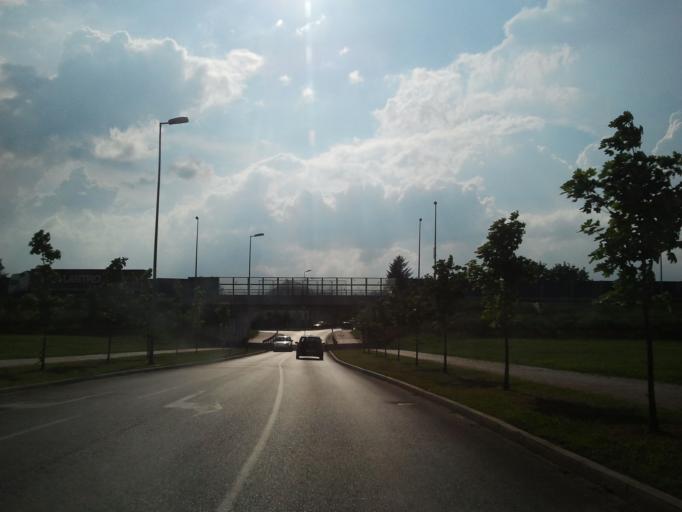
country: HR
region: Osjecko-Baranjska
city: Visnjevac
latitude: 45.5626
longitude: 18.6316
